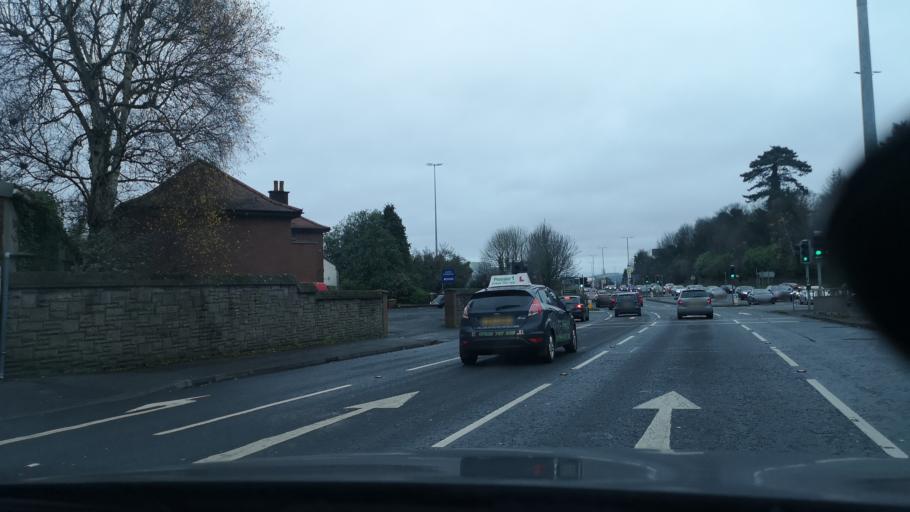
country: GB
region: Northern Ireland
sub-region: Castlereagh District
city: Castlereagh
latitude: 54.5610
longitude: -5.9103
